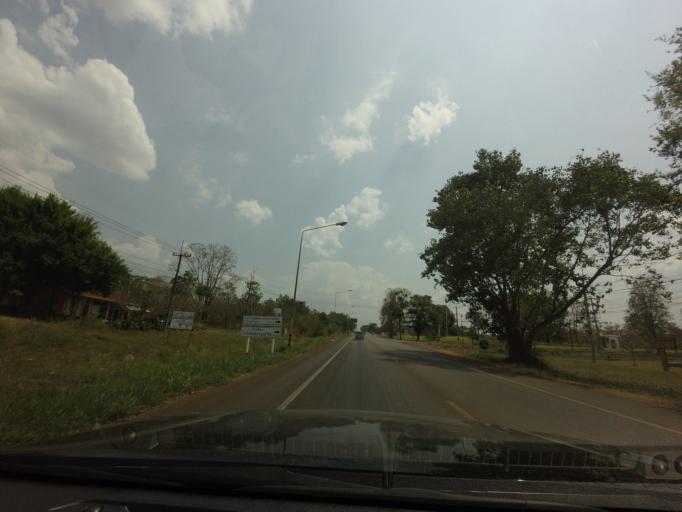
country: TH
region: Kanchanaburi
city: Sai Yok
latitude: 14.1317
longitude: 99.1607
